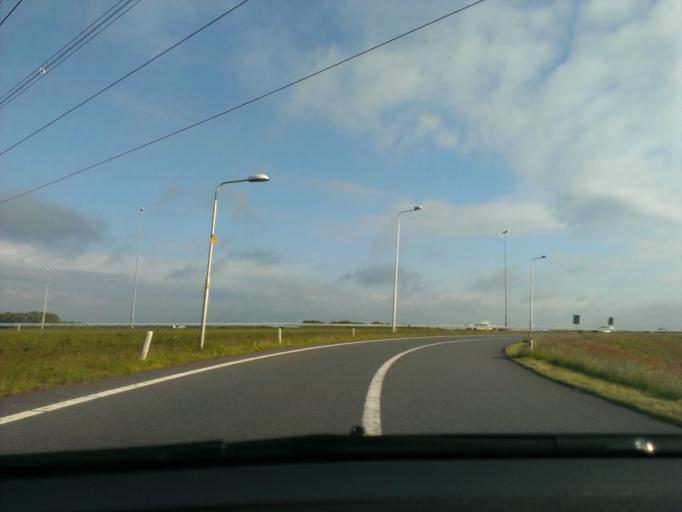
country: NL
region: Drenthe
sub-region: Gemeente Coevorden
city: Dalen
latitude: 52.7262
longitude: 6.7884
